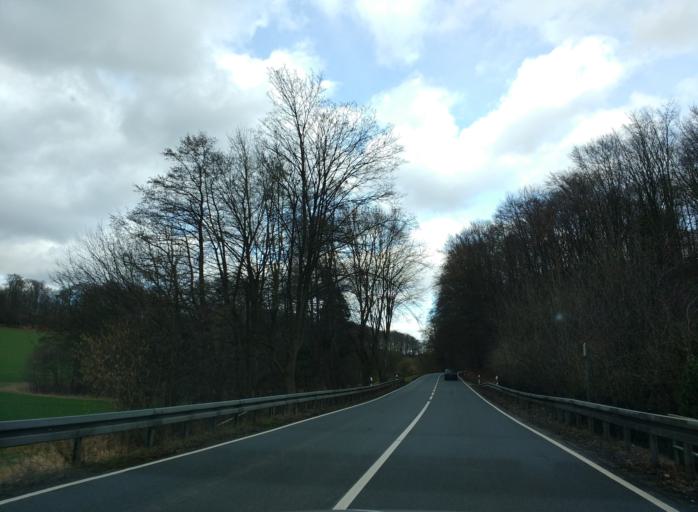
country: DE
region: North Rhine-Westphalia
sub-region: Regierungsbezirk Detmold
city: Lemgo
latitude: 52.0649
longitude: 8.9097
